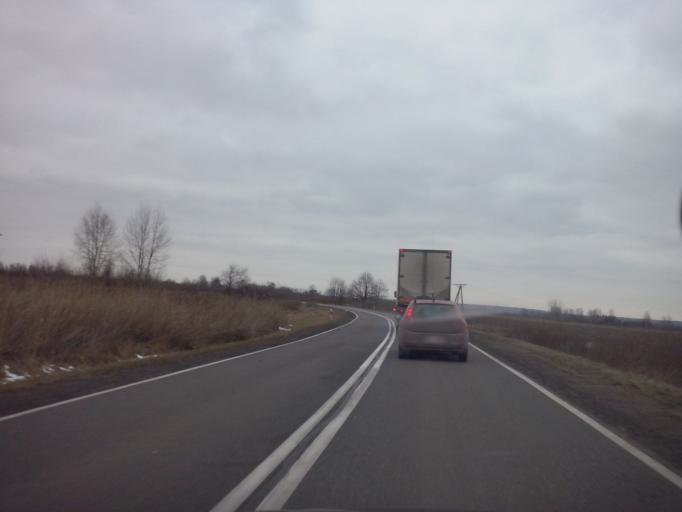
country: PL
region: Subcarpathian Voivodeship
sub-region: Powiat nizanski
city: Rudnik nad Sanem
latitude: 50.4657
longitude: 22.2427
